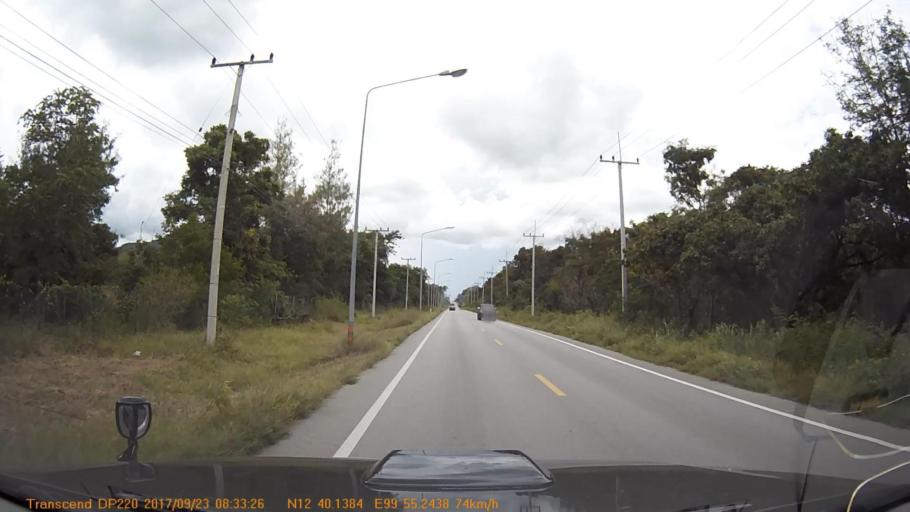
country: TH
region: Prachuap Khiri Khan
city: Hua Hin
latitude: 12.6690
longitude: 99.9206
